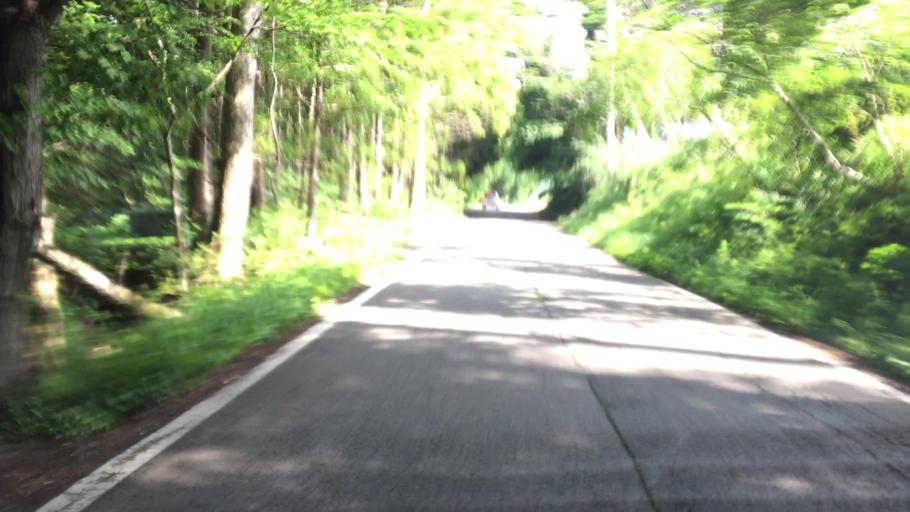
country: JP
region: Tochigi
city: Kuroiso
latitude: 37.0560
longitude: 139.9425
